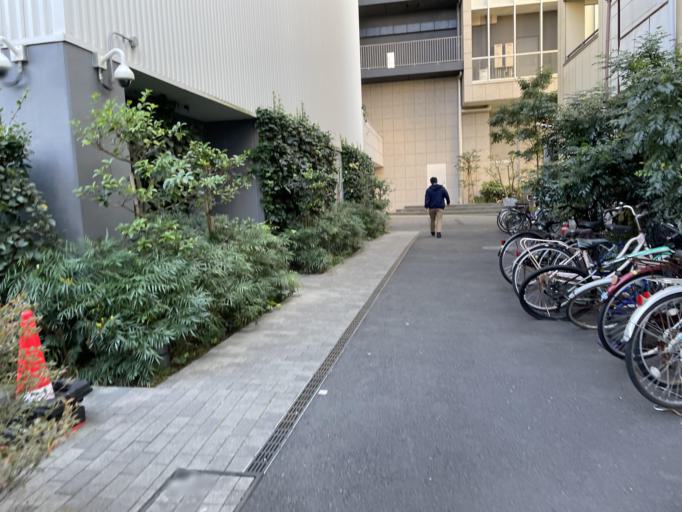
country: JP
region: Chiba
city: Matsudo
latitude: 35.7319
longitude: 139.8820
